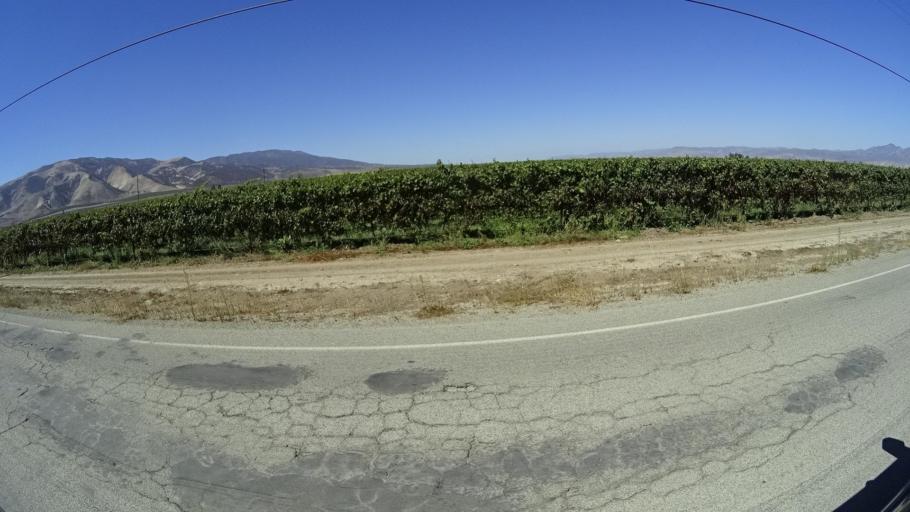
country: US
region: California
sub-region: Monterey County
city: Greenfield
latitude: 36.2931
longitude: -121.2829
